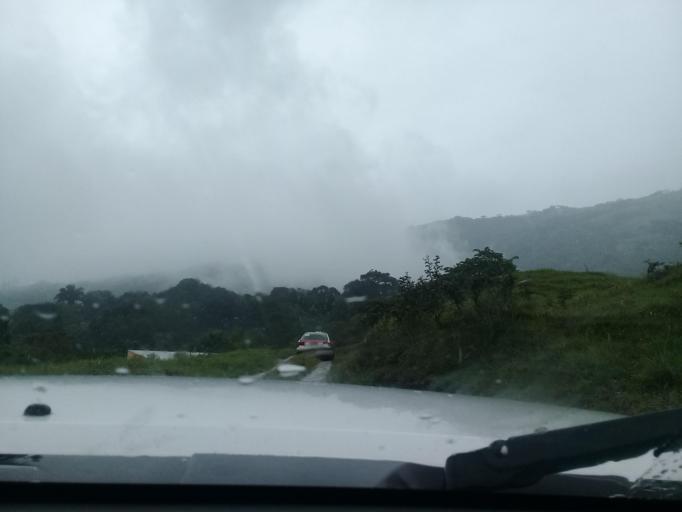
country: MX
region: Veracruz
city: Santiago Tuxtla
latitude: 18.4574
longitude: -95.3262
